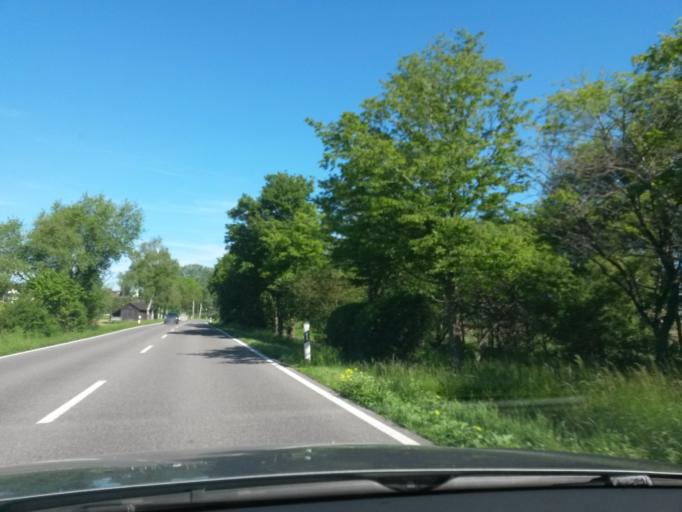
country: DE
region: Baden-Wuerttemberg
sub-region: Tuebingen Region
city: Durnau
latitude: 48.0726
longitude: 9.5634
